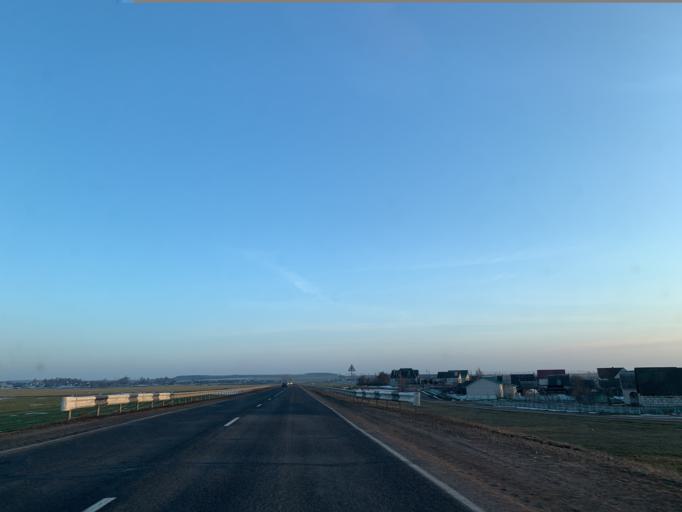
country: BY
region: Minsk
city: Haradzyeya
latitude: 53.3129
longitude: 26.5651
